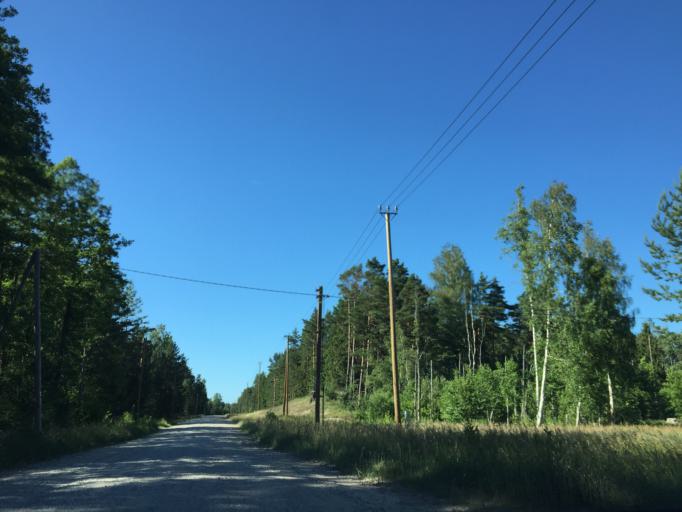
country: LV
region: Ventspils
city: Ventspils
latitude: 57.5645
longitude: 21.7248
